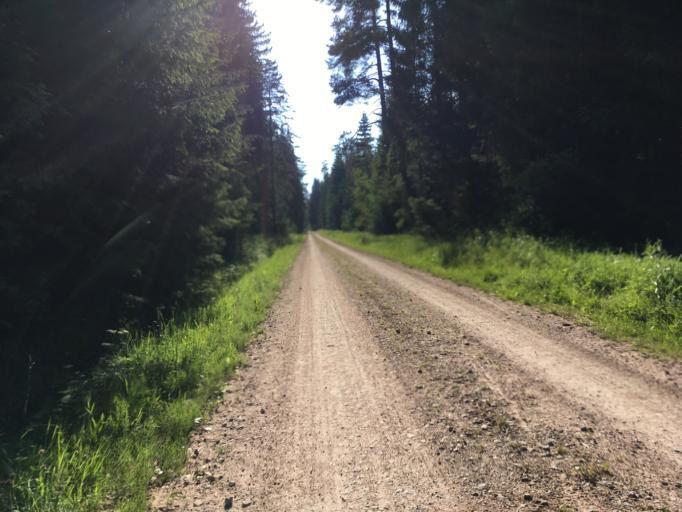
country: DE
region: Baden-Wuerttemberg
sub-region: Freiburg Region
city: Eisenbach
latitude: 47.9362
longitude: 8.2997
